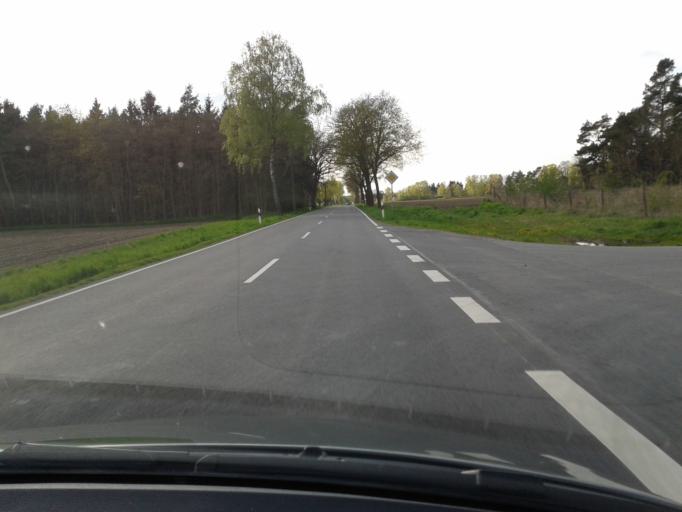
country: DE
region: Lower Saxony
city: Lubbow
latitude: 52.9139
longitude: 11.1612
